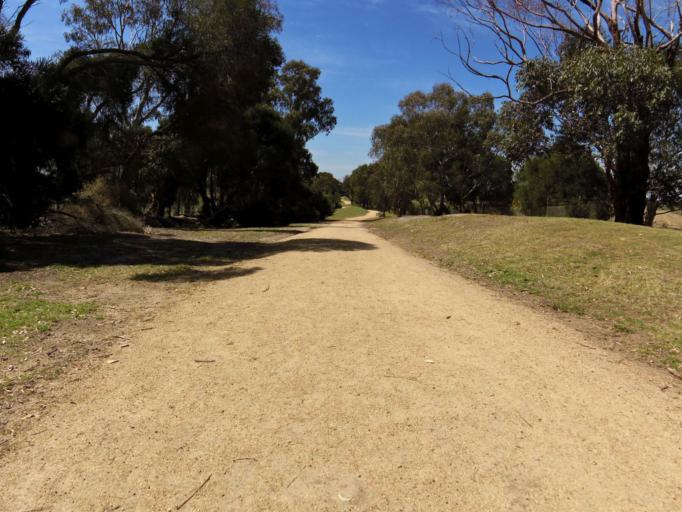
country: AU
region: Victoria
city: Heatherton
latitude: -37.9512
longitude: 145.0930
